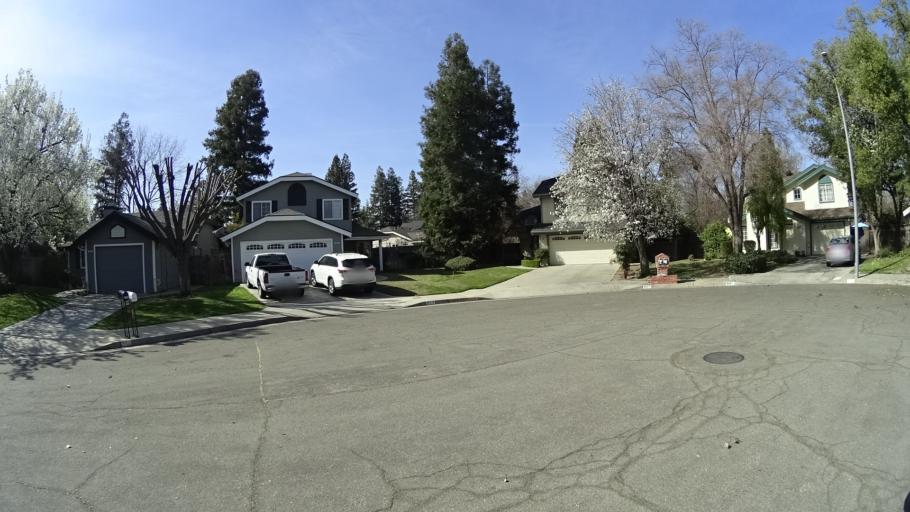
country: US
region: California
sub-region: Fresno County
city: Clovis
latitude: 36.8827
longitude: -119.7684
